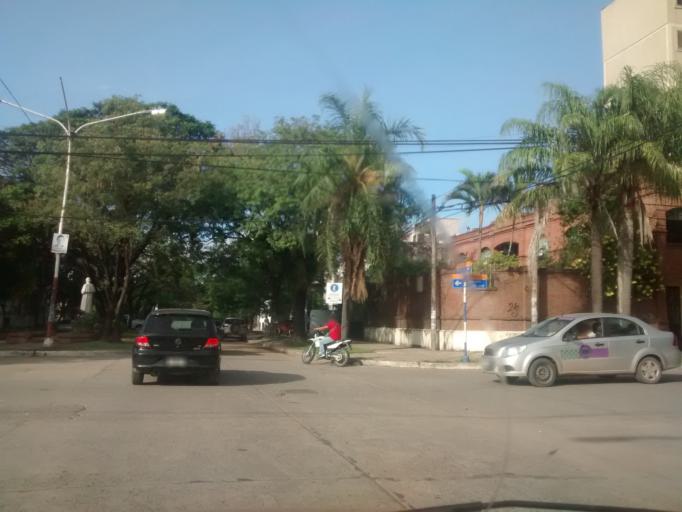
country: AR
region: Chaco
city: Resistencia
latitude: -27.4518
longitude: -58.9786
